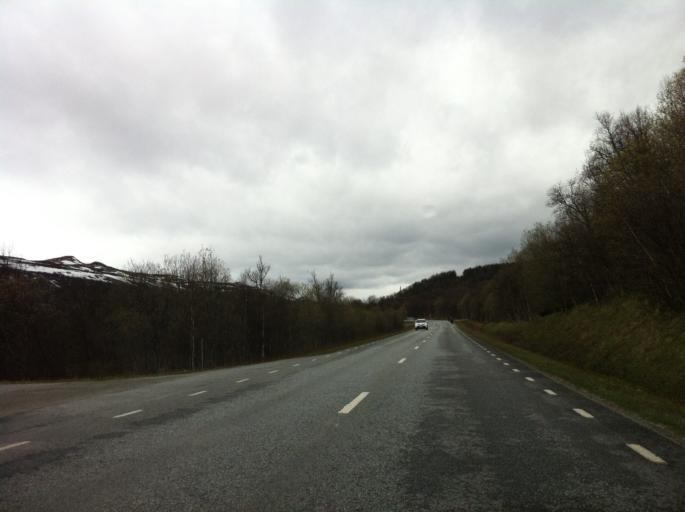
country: NO
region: Sor-Trondelag
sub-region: Tydal
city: Aas
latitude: 62.5528
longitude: 12.2881
